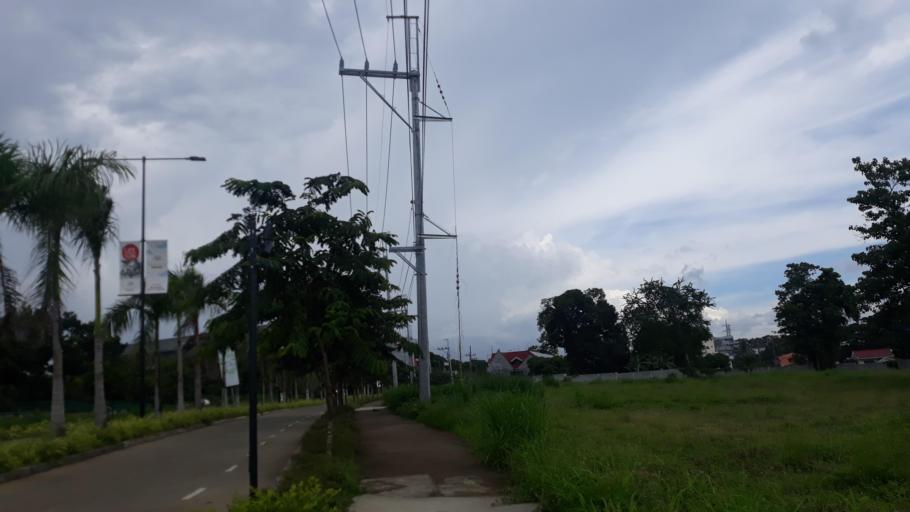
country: PH
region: Calabarzon
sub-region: Province of Cavite
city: Dasmarinas
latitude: 14.3020
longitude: 120.9480
